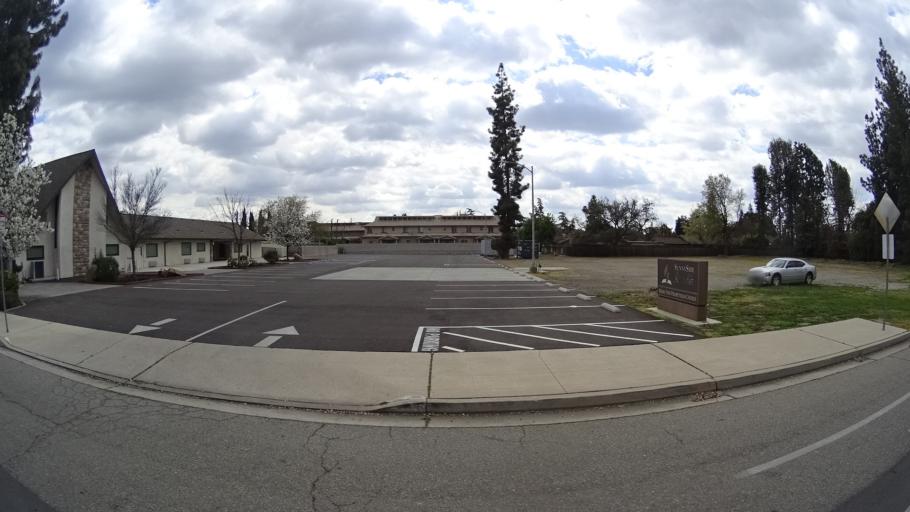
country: US
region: California
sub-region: Fresno County
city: Fresno
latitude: 36.8156
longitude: -119.8004
